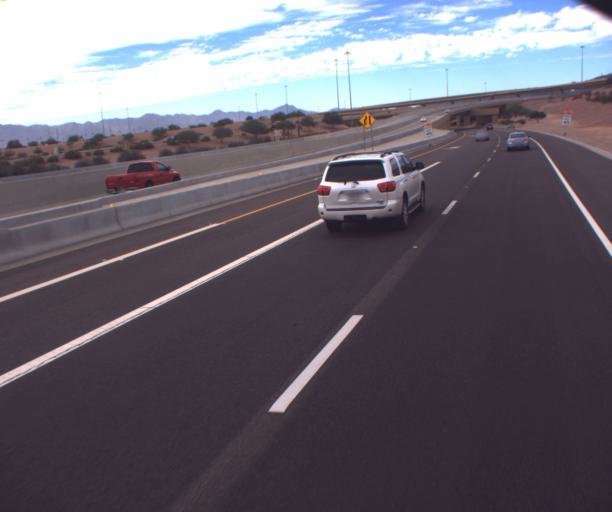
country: US
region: Arizona
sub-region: Maricopa County
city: Guadalupe
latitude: 33.2965
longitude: -111.9667
